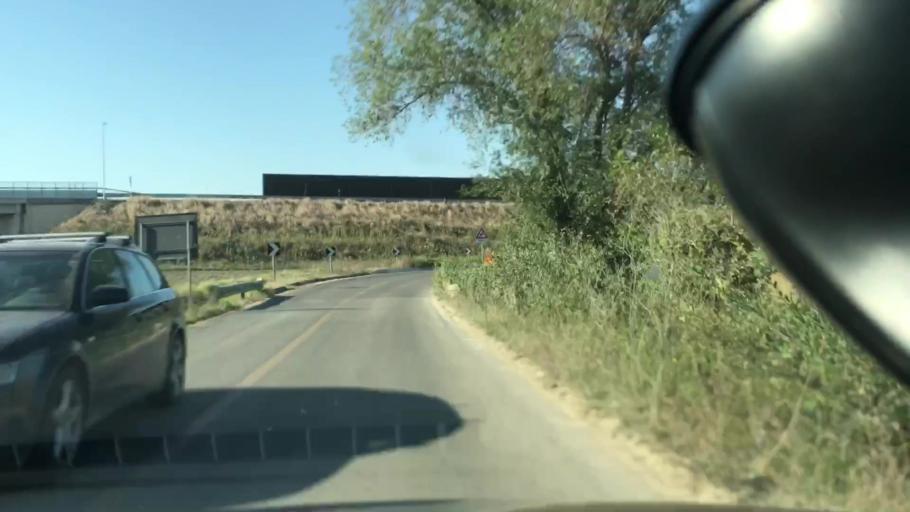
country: IT
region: Basilicate
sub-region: Provincia di Matera
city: La Martella
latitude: 40.6581
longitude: 16.5612
